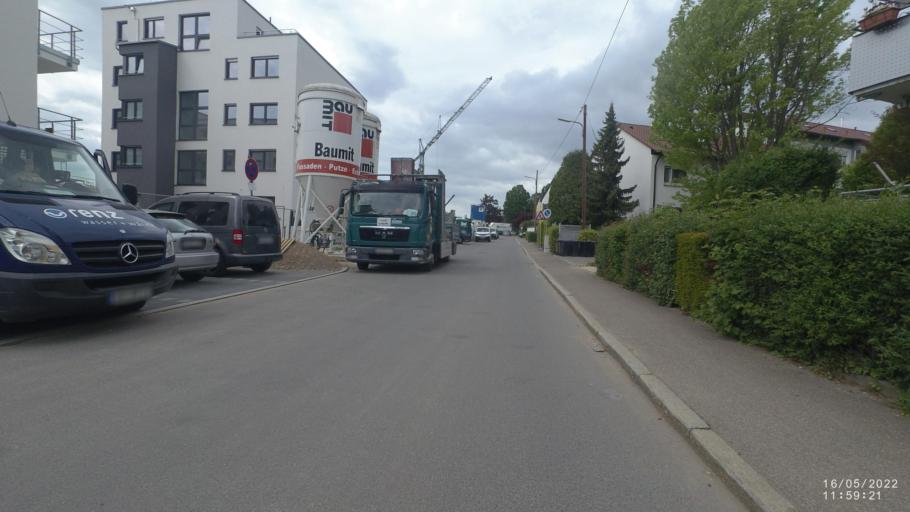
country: DE
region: Baden-Wuerttemberg
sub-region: Regierungsbezirk Stuttgart
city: Fellbach
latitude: 48.8264
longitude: 9.2650
